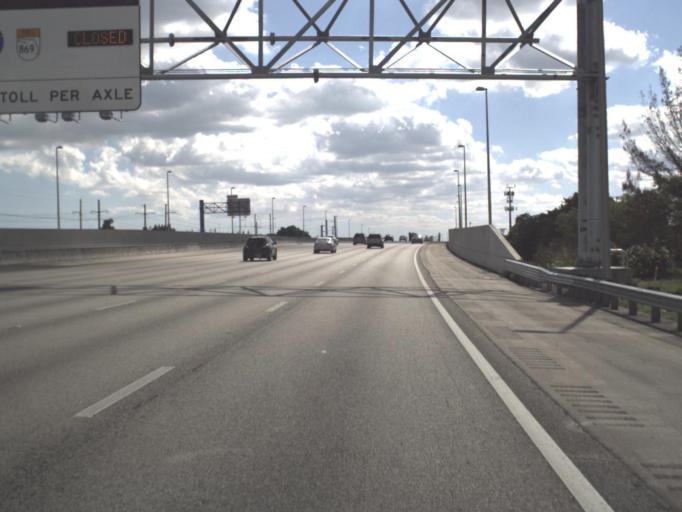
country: US
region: Florida
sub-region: Broward County
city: Lauderhill
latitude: 26.1244
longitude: -80.2178
